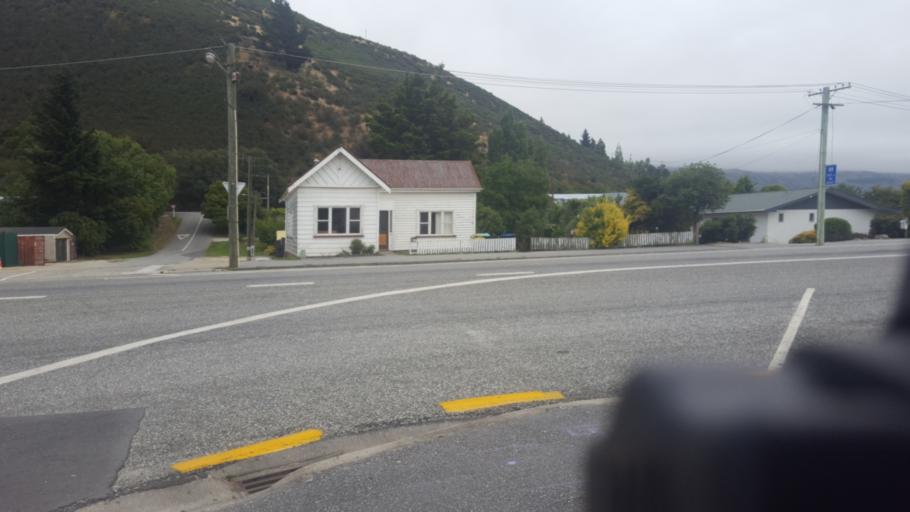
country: NZ
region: Otago
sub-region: Queenstown-Lakes District
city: Kingston
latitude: -45.5429
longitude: 169.3150
